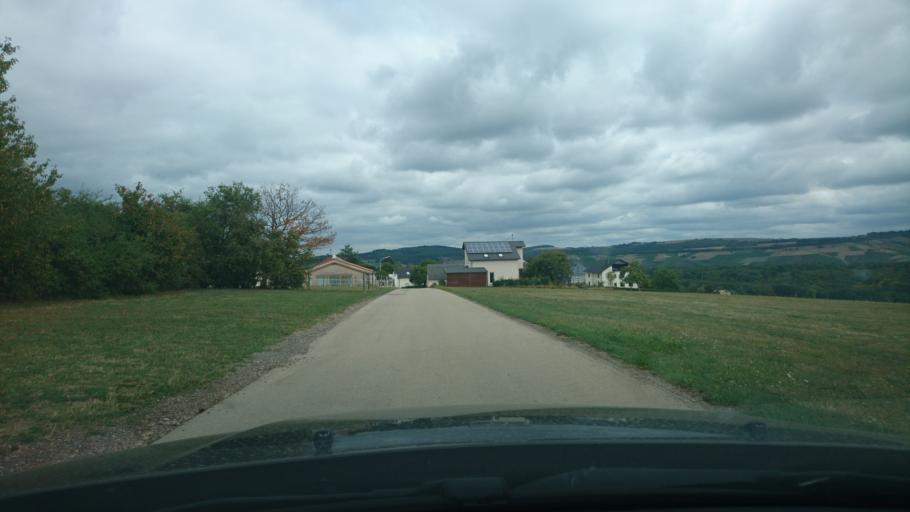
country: DE
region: Rheinland-Pfalz
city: Wiltingen
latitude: 49.6794
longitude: 6.6064
